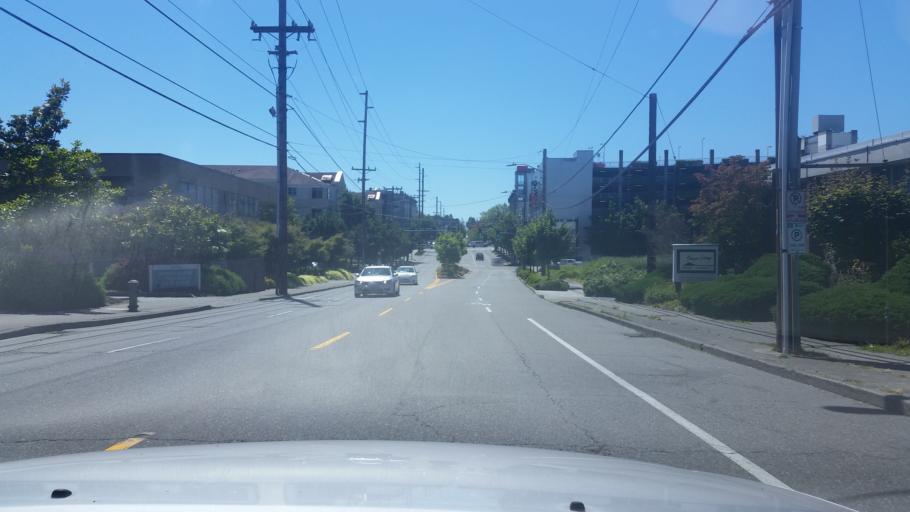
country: US
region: Washington
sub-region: King County
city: Shoreline
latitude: 47.7108
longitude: -122.3234
